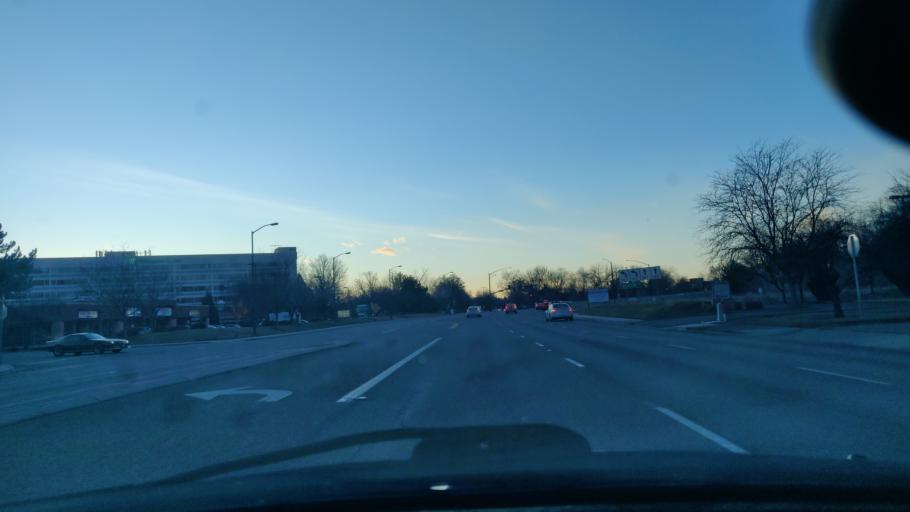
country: US
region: Idaho
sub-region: Ada County
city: Boise
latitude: 43.5987
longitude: -116.1847
